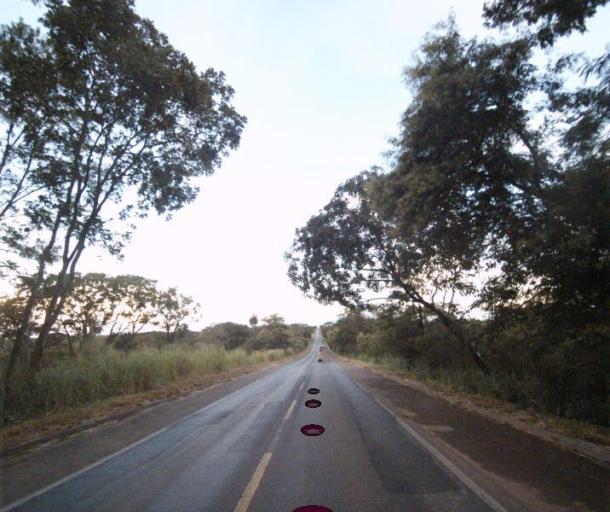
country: BR
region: Goias
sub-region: Uruacu
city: Uruacu
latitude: -14.4133
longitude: -49.1573
